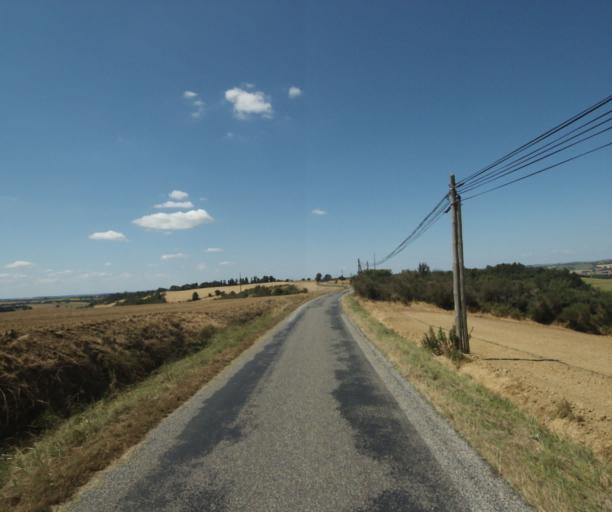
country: FR
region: Midi-Pyrenees
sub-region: Departement de la Haute-Garonne
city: Saint-Felix-Lauragais
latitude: 43.4573
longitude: 1.8834
